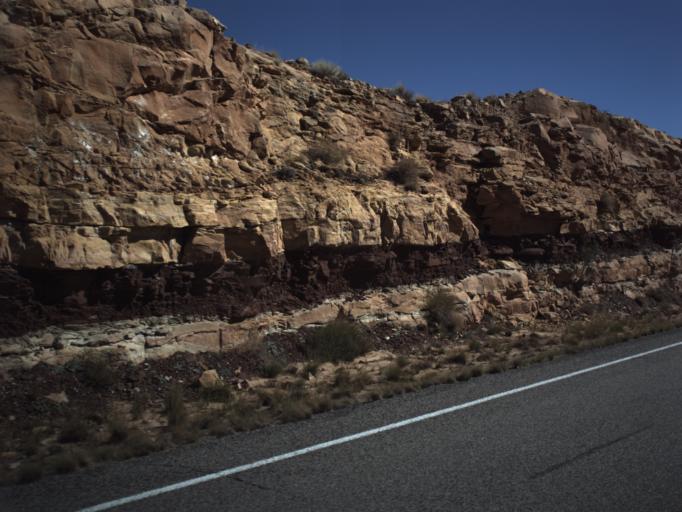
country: US
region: Utah
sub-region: San Juan County
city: Blanding
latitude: 37.8206
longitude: -110.3530
